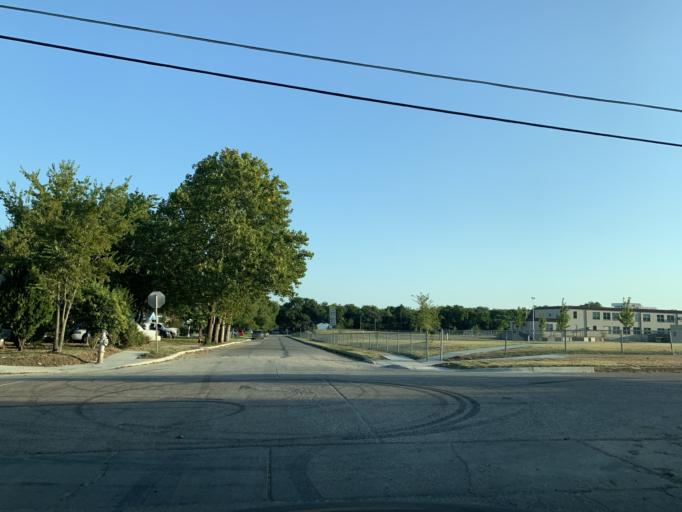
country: US
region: Texas
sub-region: Dallas County
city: Dallas
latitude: 32.7097
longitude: -96.8108
